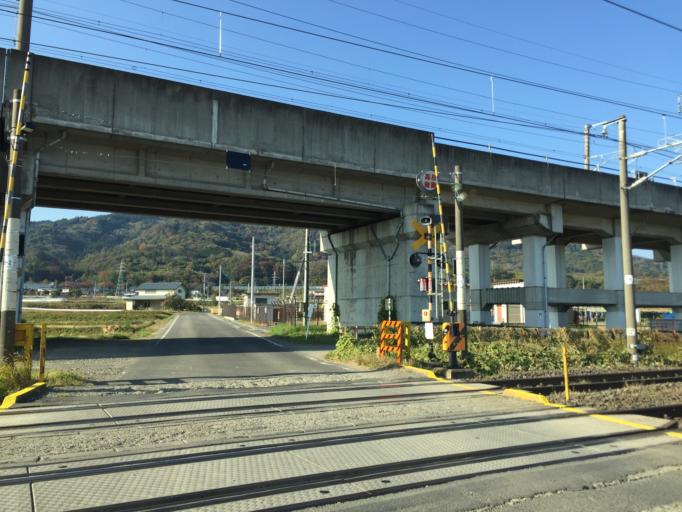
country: JP
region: Fukushima
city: Hobaramachi
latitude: 37.8320
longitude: 140.4995
